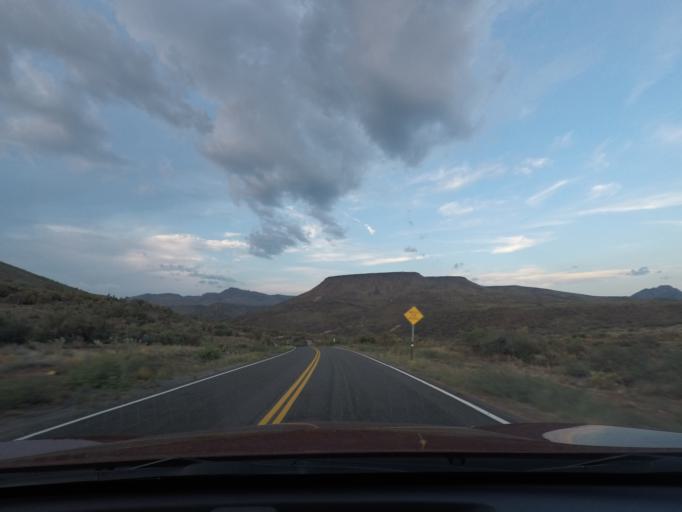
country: US
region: Arizona
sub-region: Yavapai County
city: Congress
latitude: 34.4750
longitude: -112.8249
